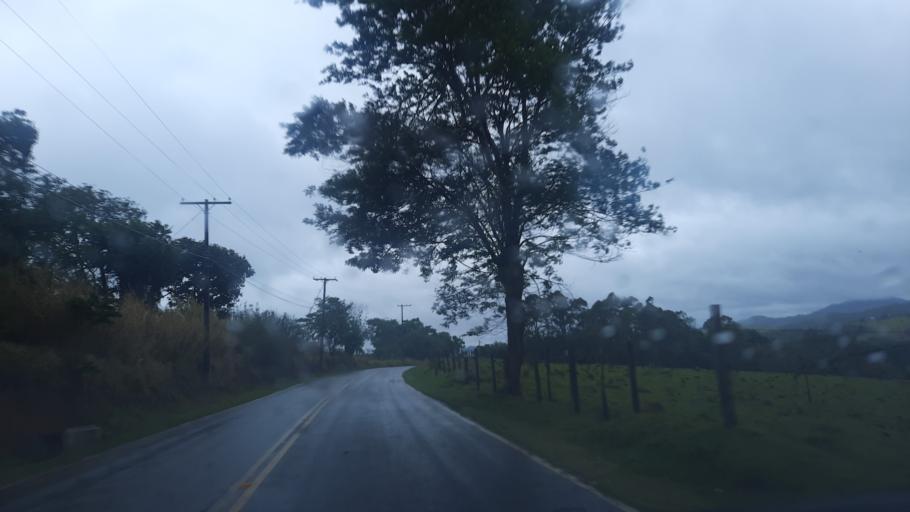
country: BR
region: Sao Paulo
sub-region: Atibaia
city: Atibaia
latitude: -23.0736
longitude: -46.5184
